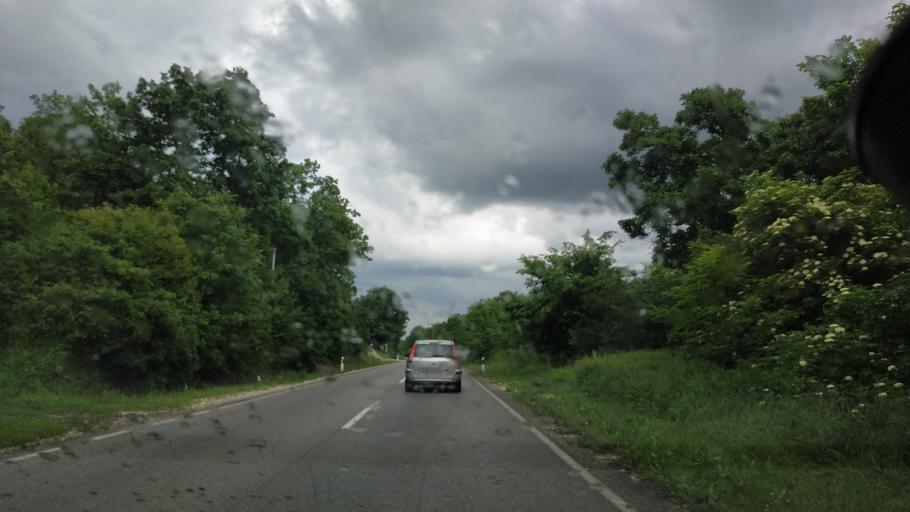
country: RS
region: Central Serbia
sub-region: Borski Okrug
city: Bor
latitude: 44.0560
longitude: 22.0686
